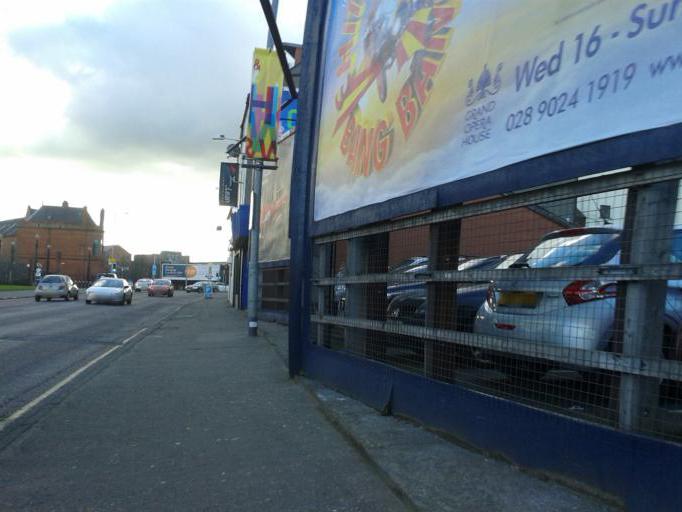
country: GB
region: Northern Ireland
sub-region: City of Belfast
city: Belfast
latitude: 54.5929
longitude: -5.9254
